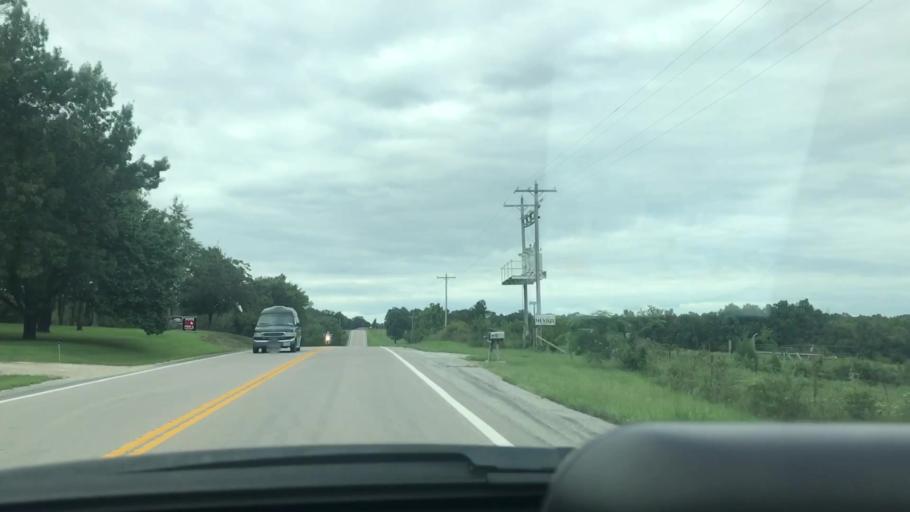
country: US
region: Missouri
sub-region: Benton County
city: Warsaw
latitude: 38.1482
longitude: -93.2923
